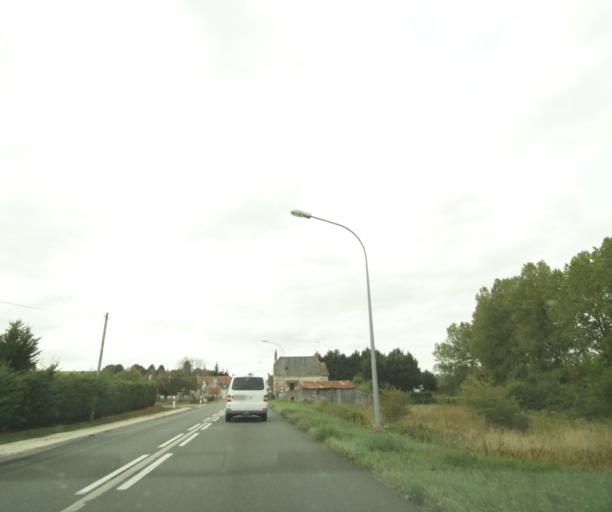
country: FR
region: Centre
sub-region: Departement d'Indre-et-Loire
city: Perrusson
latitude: 47.0580
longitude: 1.0852
